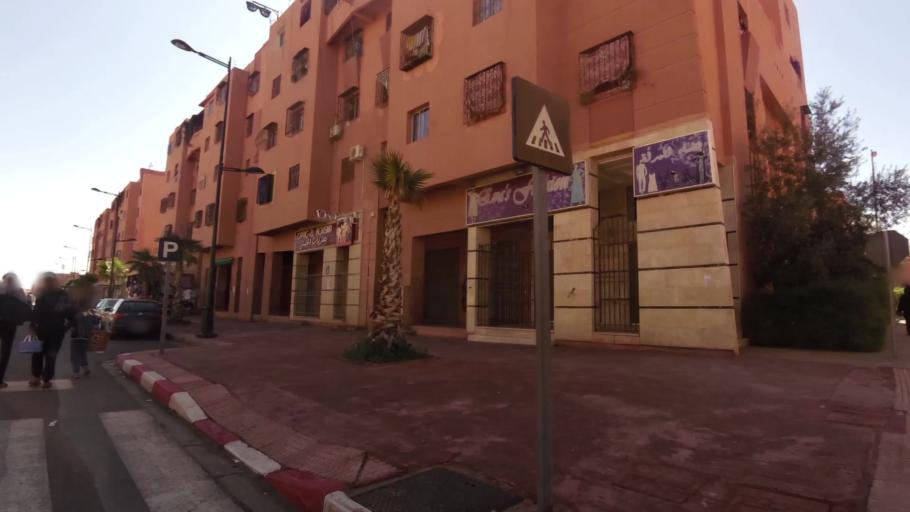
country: MA
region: Marrakech-Tensift-Al Haouz
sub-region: Marrakech
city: Marrakesh
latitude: 31.5919
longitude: -8.0478
